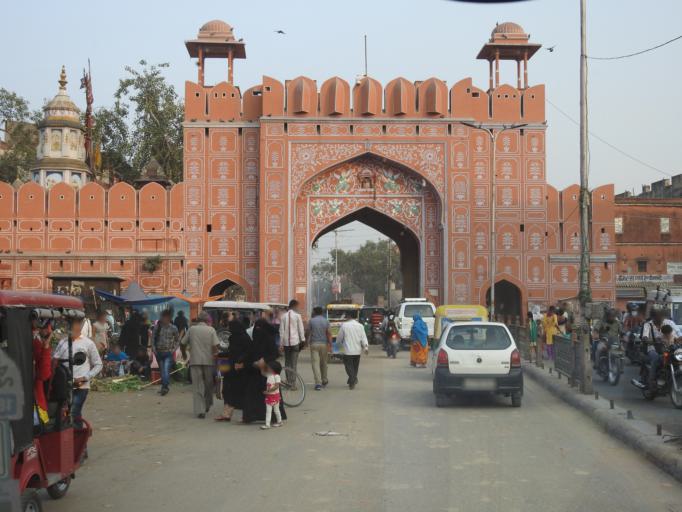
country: IN
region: Rajasthan
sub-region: Jaipur
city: Jaipur
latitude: 26.9267
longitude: 75.8091
